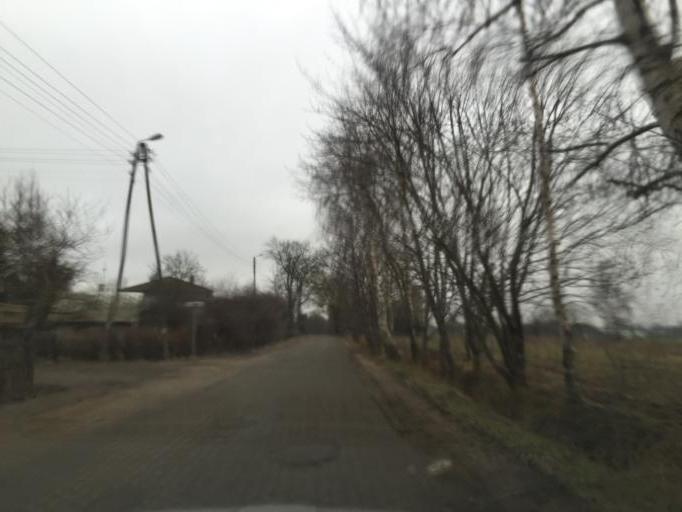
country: PL
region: Pomeranian Voivodeship
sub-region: Powiat kartuski
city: Chwaszczyno
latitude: 54.4122
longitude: 18.4455
